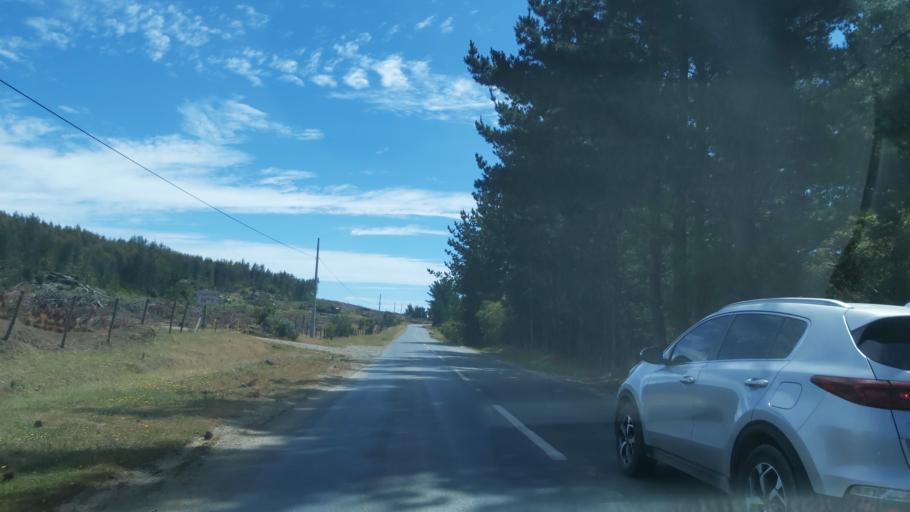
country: CL
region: Maule
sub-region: Provincia de Talca
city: Constitucion
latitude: -35.5383
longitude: -72.5496
